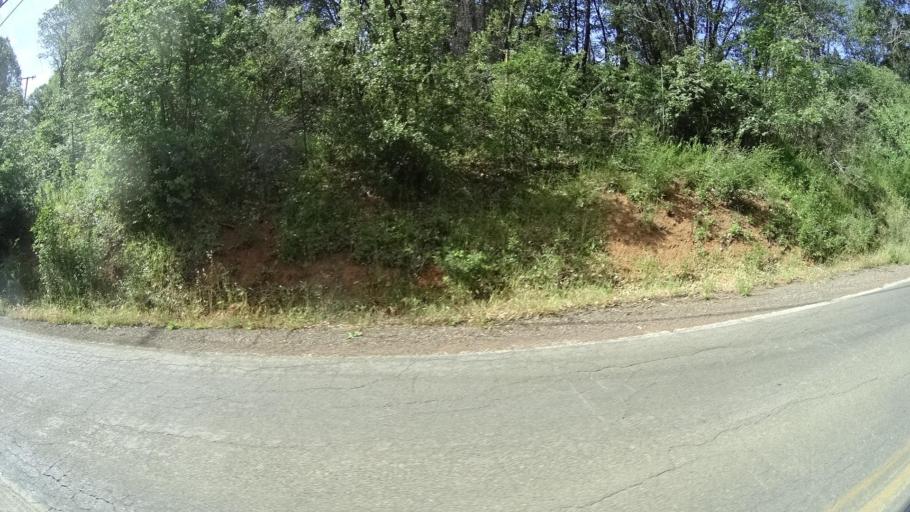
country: US
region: California
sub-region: Lake County
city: Soda Bay
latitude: 38.9151
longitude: -122.7527
